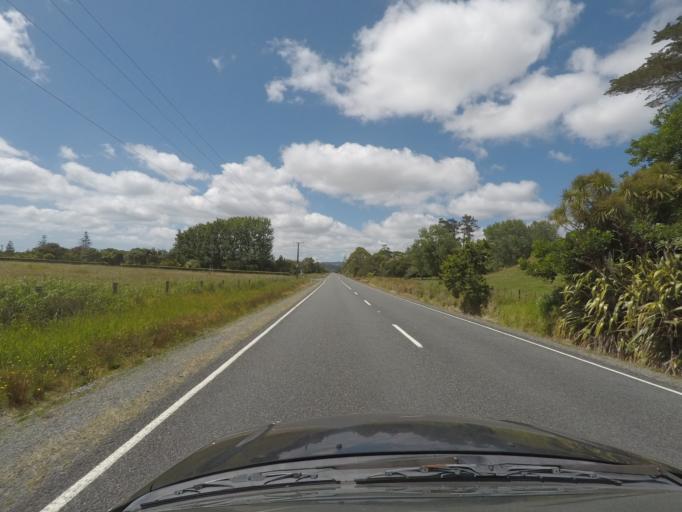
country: NZ
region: Northland
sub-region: Whangarei
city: Ruakaka
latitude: -35.9969
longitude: 174.4730
